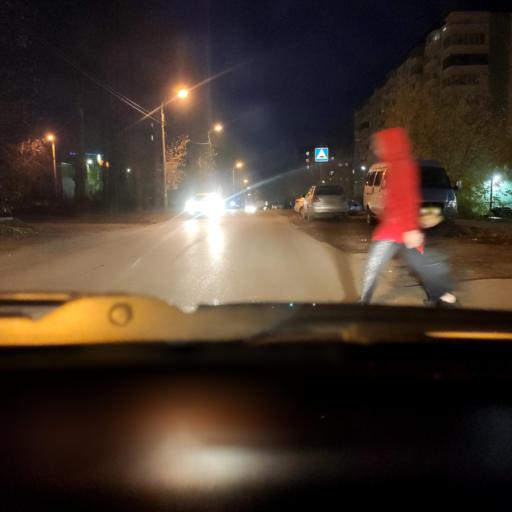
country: RU
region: Perm
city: Perm
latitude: 58.1027
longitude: 56.3045
